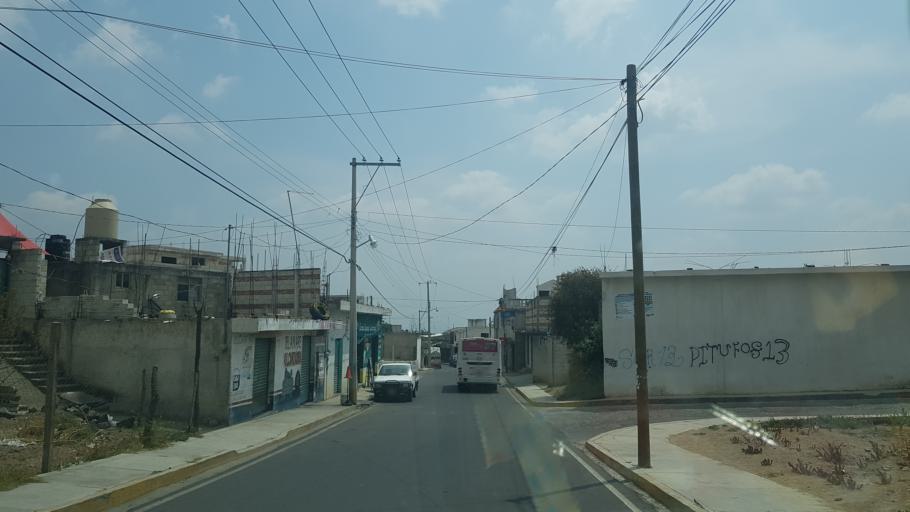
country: MX
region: Puebla
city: Domingo Arenas
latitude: 19.1405
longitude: -98.4613
